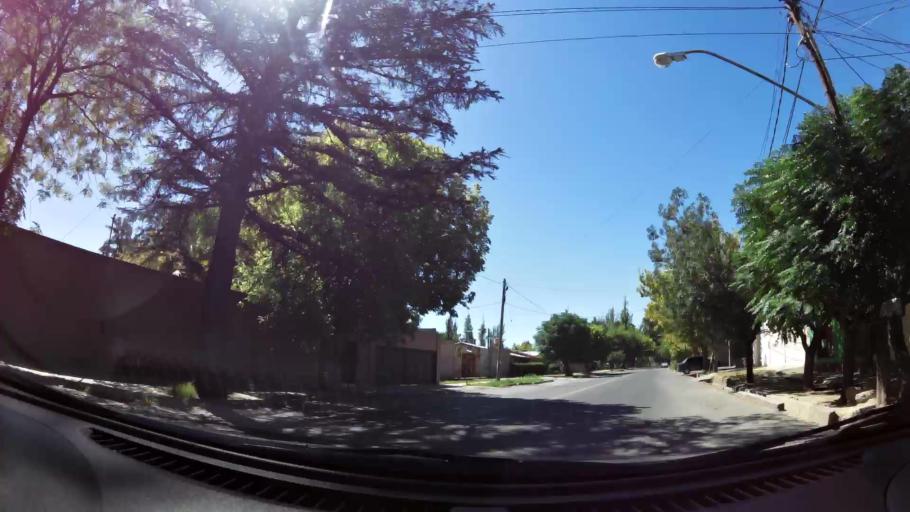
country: AR
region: Mendoza
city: Las Heras
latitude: -32.8239
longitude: -68.8377
